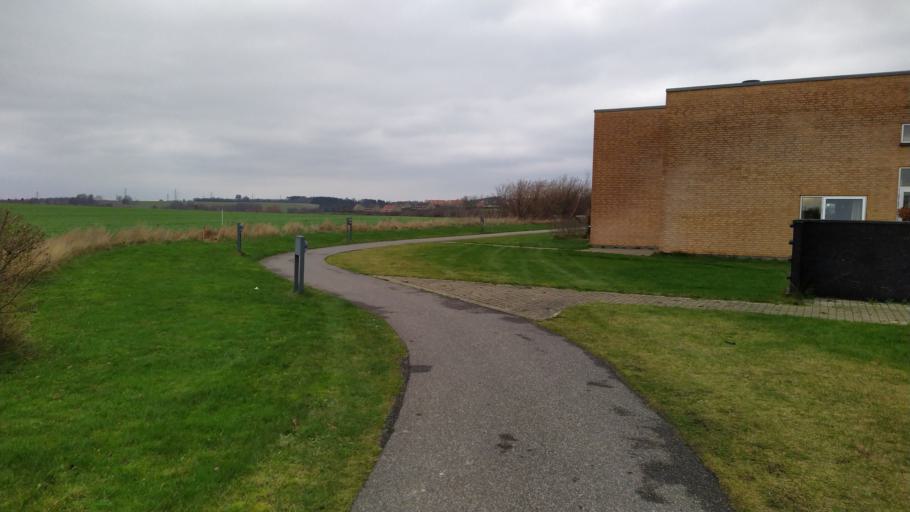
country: DK
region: Capital Region
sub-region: Egedal Kommune
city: Vekso
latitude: 55.7478
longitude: 12.2352
